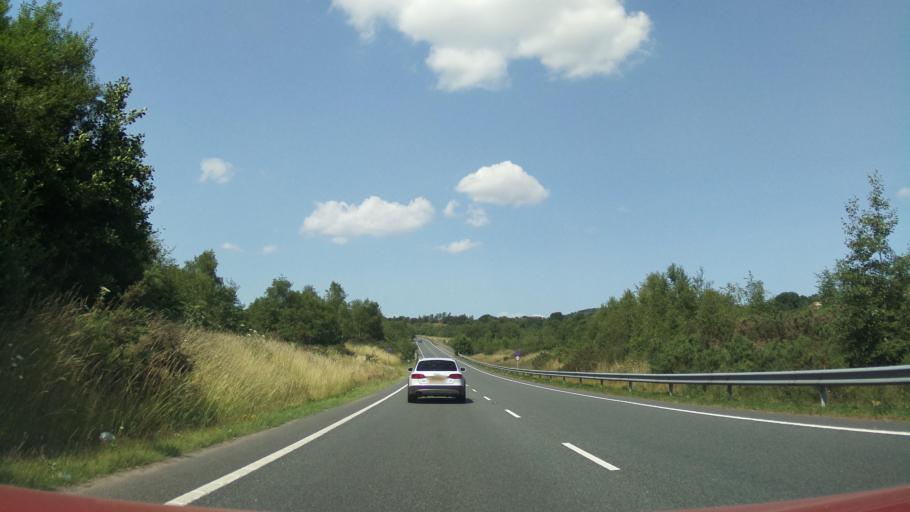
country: GB
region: Wales
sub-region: Caerphilly County Borough
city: Bargoed
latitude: 51.6770
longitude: -3.2236
